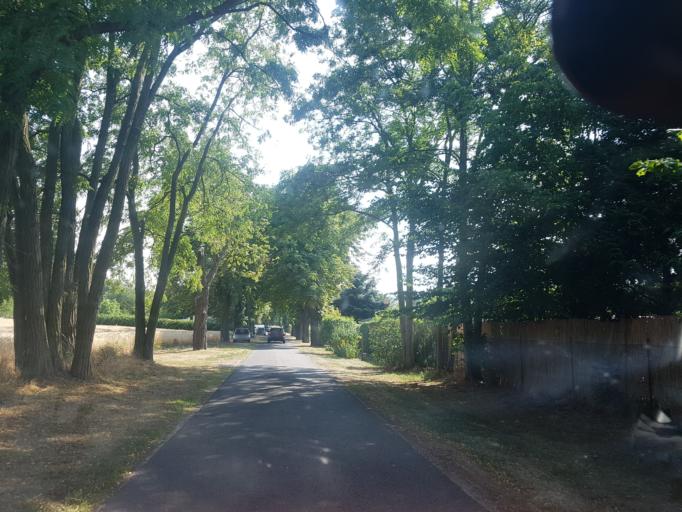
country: DE
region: Brandenburg
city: Ludwigsfelde
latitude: 52.2739
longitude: 13.2856
